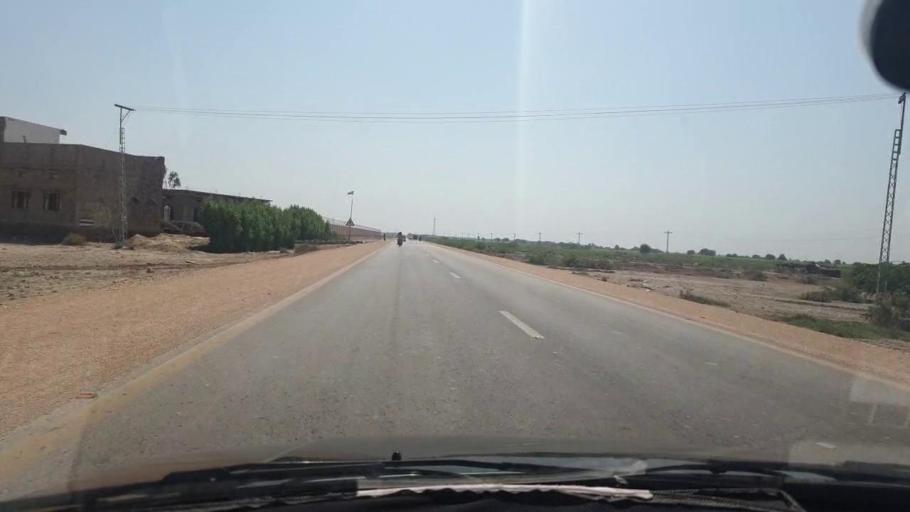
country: PK
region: Sindh
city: Chambar
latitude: 25.3446
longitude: 68.7927
